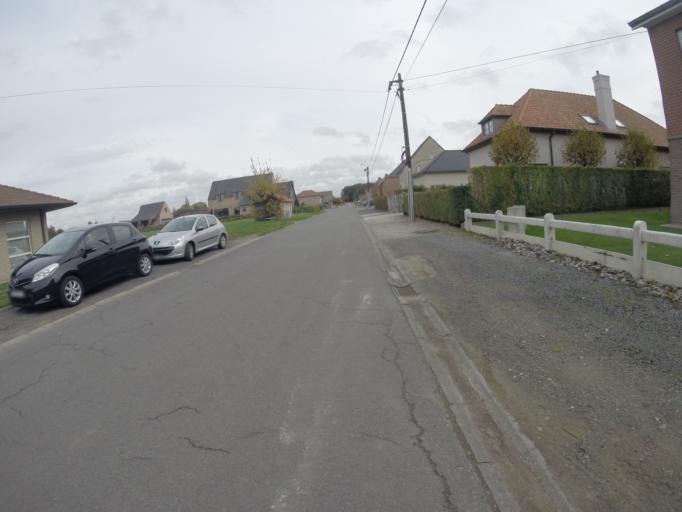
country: BE
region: Flanders
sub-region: Provincie Oost-Vlaanderen
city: Maldegem
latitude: 51.1823
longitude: 3.4439
